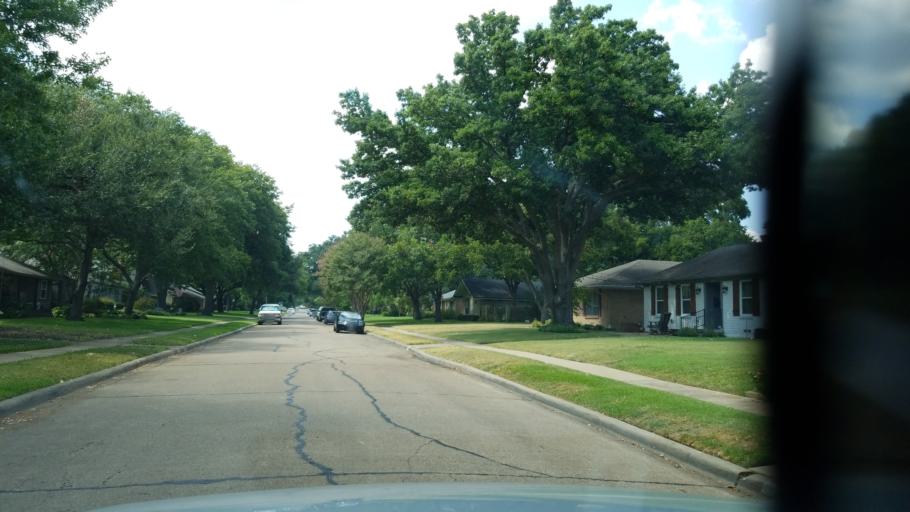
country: US
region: Texas
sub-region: Dallas County
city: Richardson
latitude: 32.9699
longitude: -96.7585
